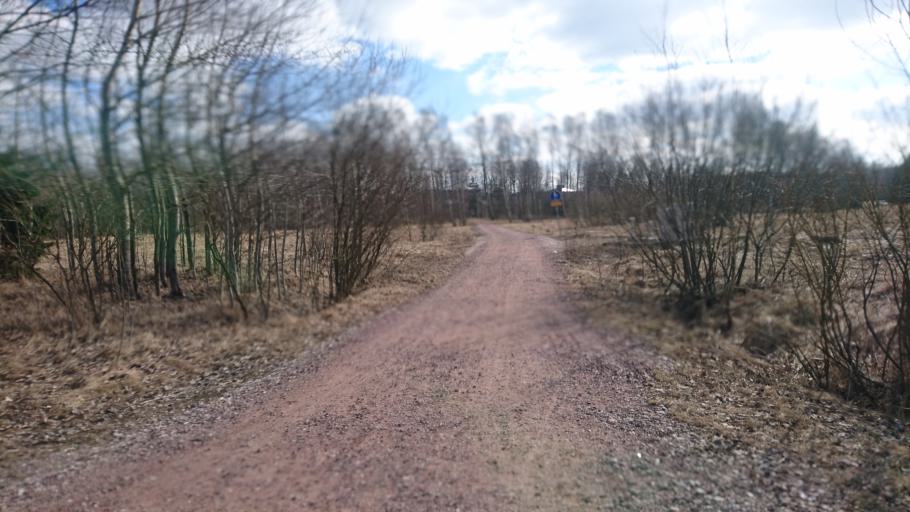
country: FI
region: Uusimaa
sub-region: Helsinki
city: Kauniainen
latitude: 60.1865
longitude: 24.7318
